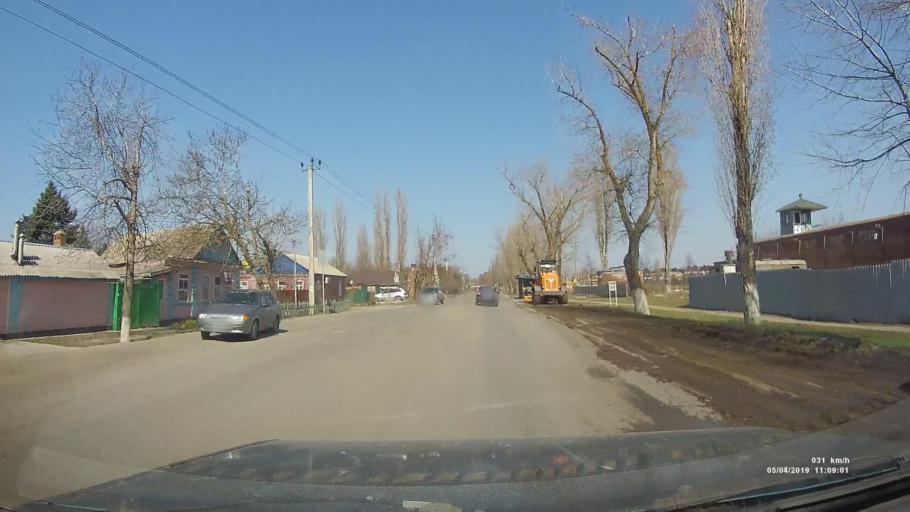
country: RU
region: Rostov
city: Azov
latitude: 47.0886
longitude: 39.4339
